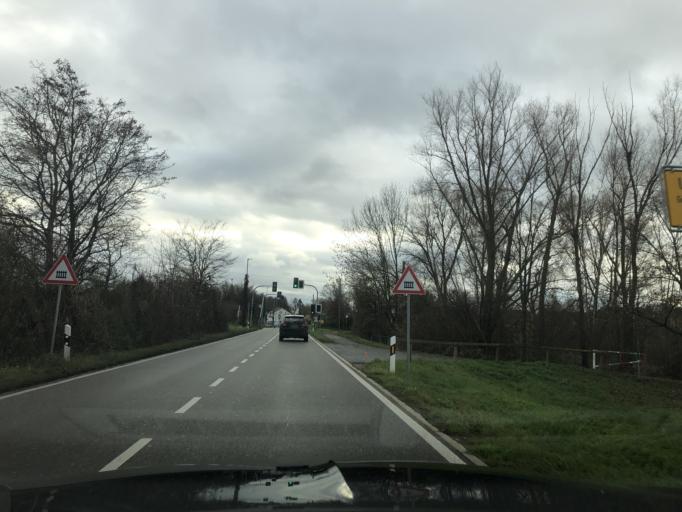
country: DE
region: Baden-Wuerttemberg
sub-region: Karlsruhe Region
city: Ubstadt-Weiher
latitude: 49.1596
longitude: 8.6264
